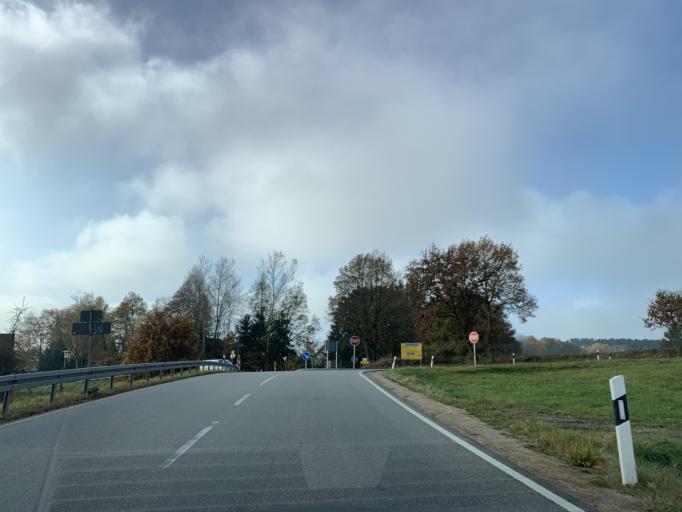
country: DE
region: Bavaria
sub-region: Upper Palatinate
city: Bruck in der Oberpfalz
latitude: 49.2646
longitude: 12.2960
